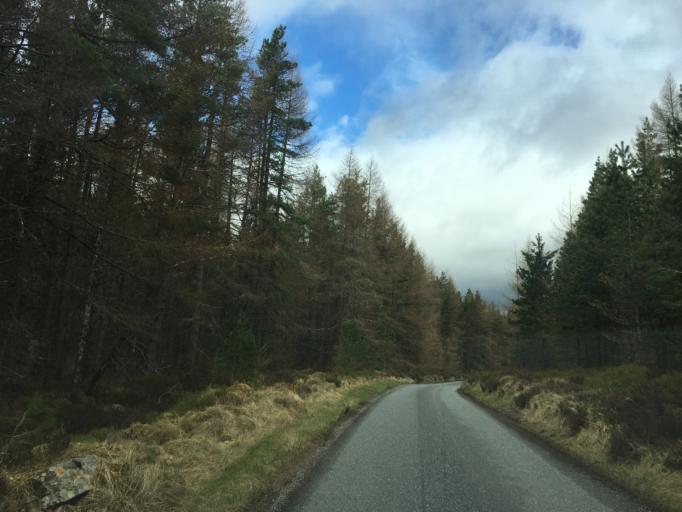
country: GB
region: Scotland
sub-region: Highland
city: Kingussie
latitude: 57.0980
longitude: -3.9202
